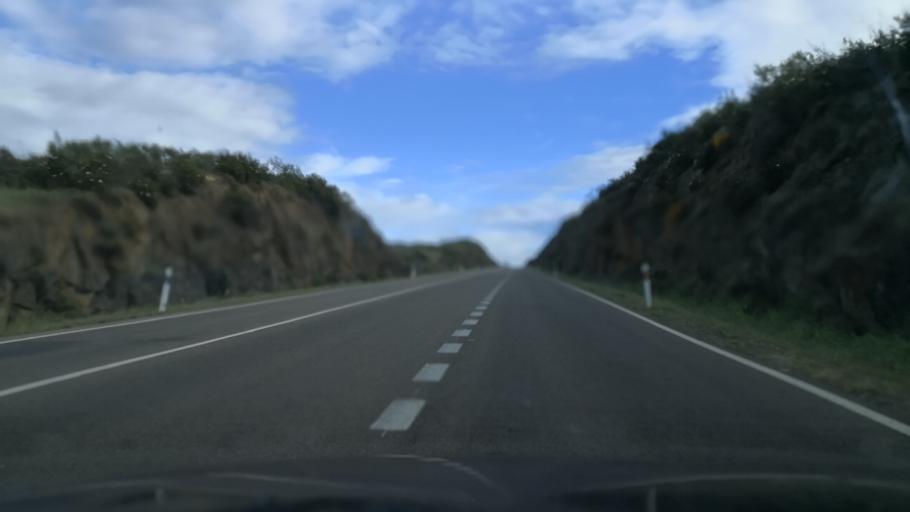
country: ES
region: Extremadura
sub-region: Provincia de Caceres
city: Coria
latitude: 39.9512
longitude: -6.5092
